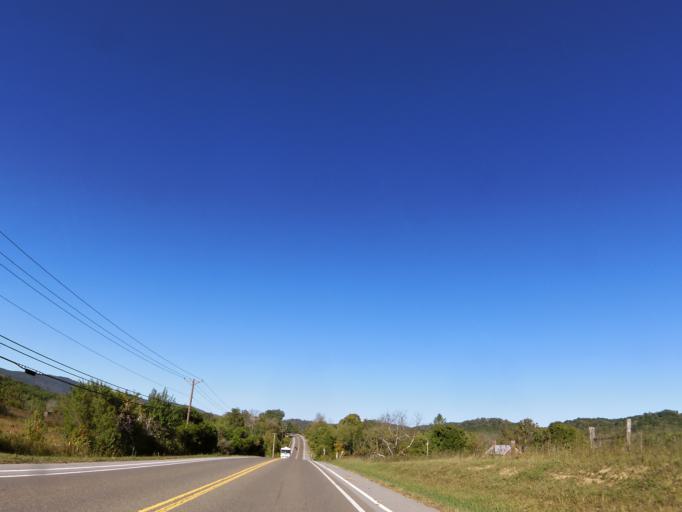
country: US
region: Tennessee
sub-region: Grainger County
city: Blaine
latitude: 36.1724
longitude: -83.6879
